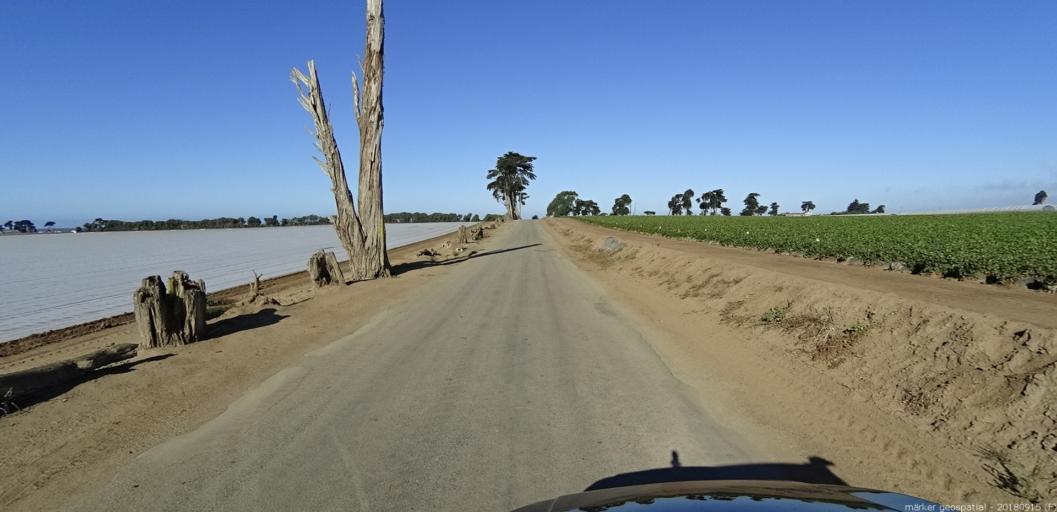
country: US
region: California
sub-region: Monterey County
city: Elkhorn
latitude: 36.8270
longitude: -121.7847
